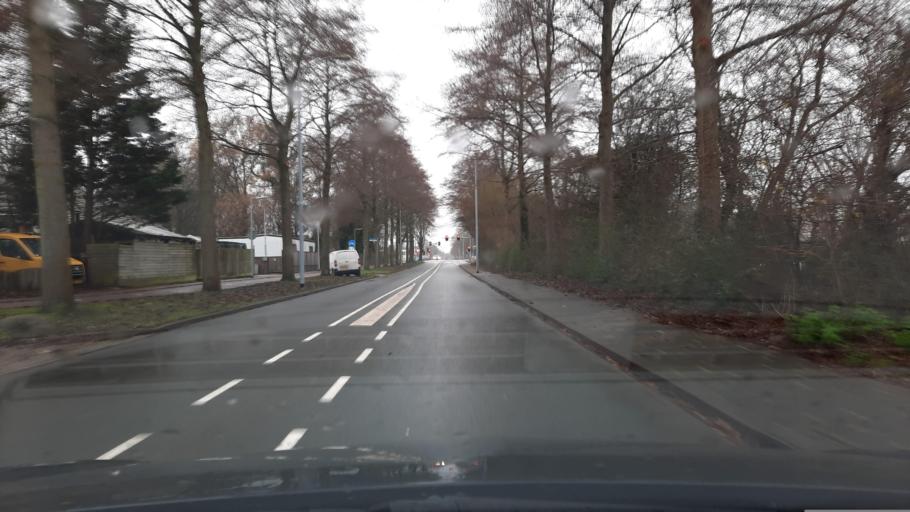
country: NL
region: South Holland
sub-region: Gemeente Kaag en Braassem
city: Oude Wetering
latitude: 52.2594
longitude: 4.6306
